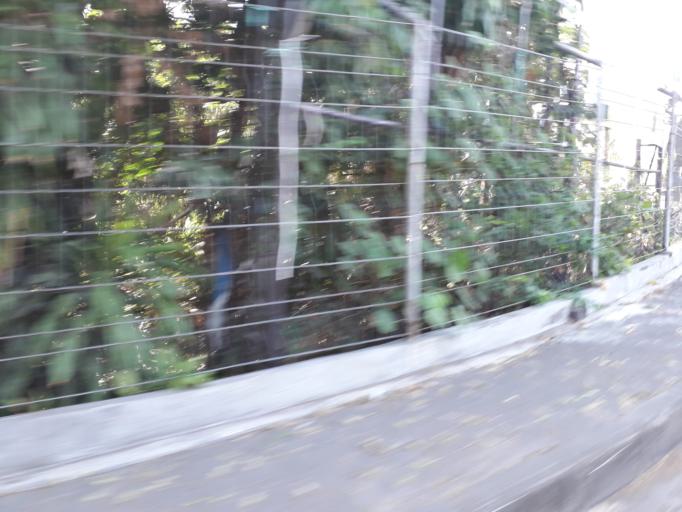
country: ID
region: Daerah Istimewa Yogyakarta
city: Yogyakarta
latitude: -7.7649
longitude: 110.3756
